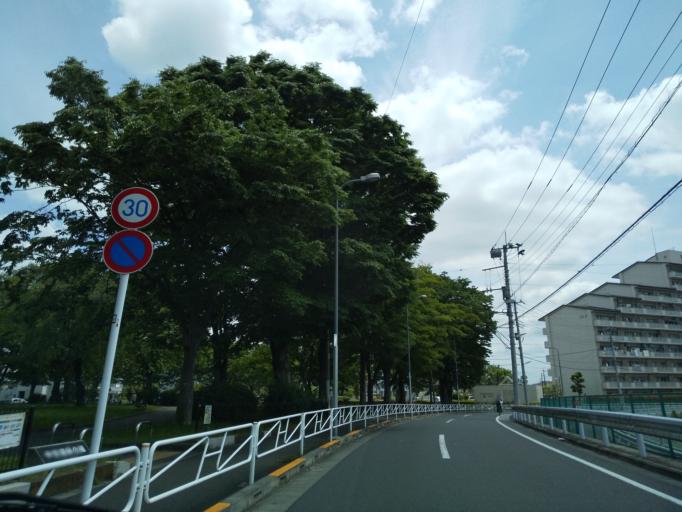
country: JP
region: Tokyo
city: Hachioji
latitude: 35.6740
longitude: 139.3231
